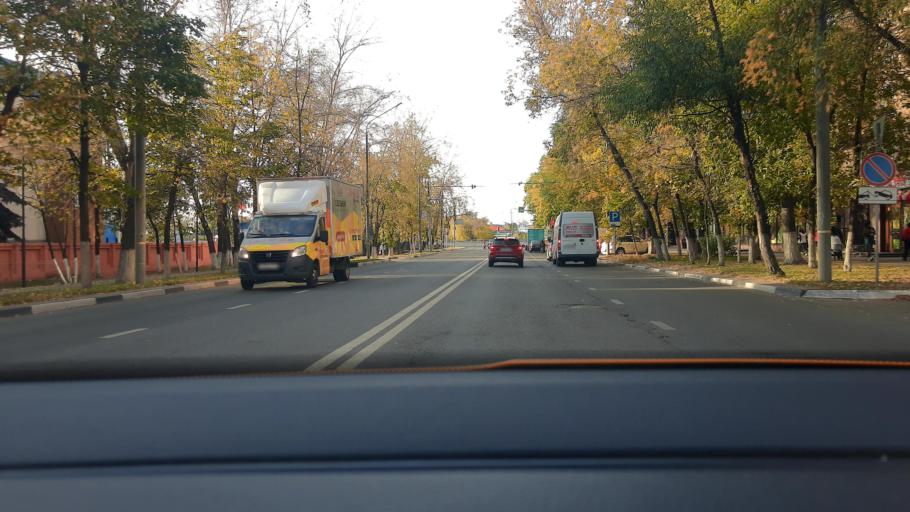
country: RU
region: Moskovskaya
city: Reutov
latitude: 55.7672
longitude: 37.8481
